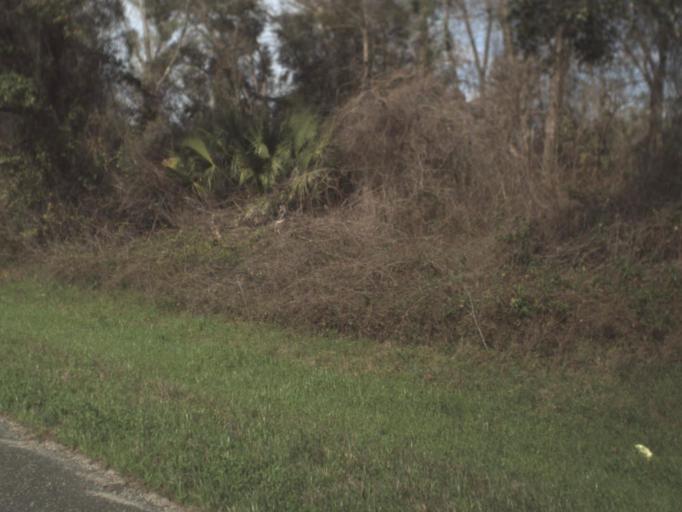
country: US
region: Florida
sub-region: Jefferson County
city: Monticello
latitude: 30.4637
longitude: -83.8920
